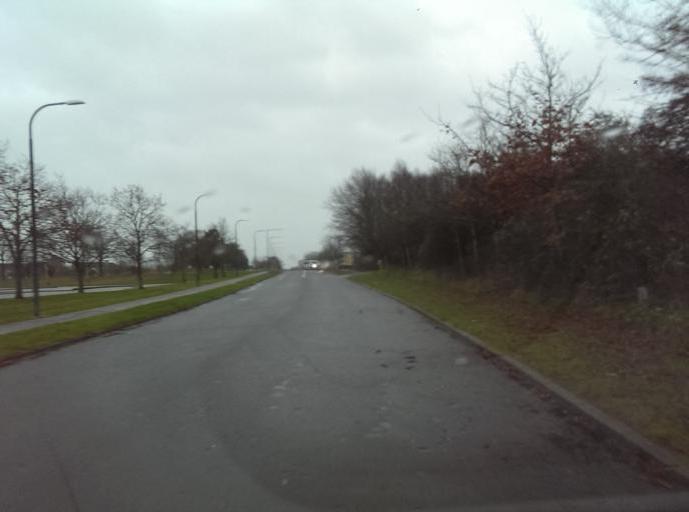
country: DK
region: South Denmark
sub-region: Esbjerg Kommune
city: Esbjerg
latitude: 55.4886
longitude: 8.4899
